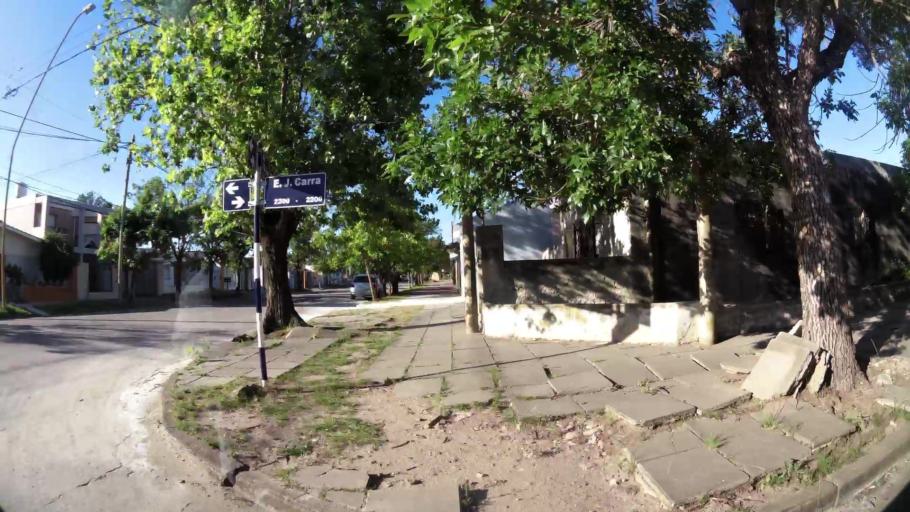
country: AR
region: Cordoba
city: San Francisco
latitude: -31.4404
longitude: -62.0943
